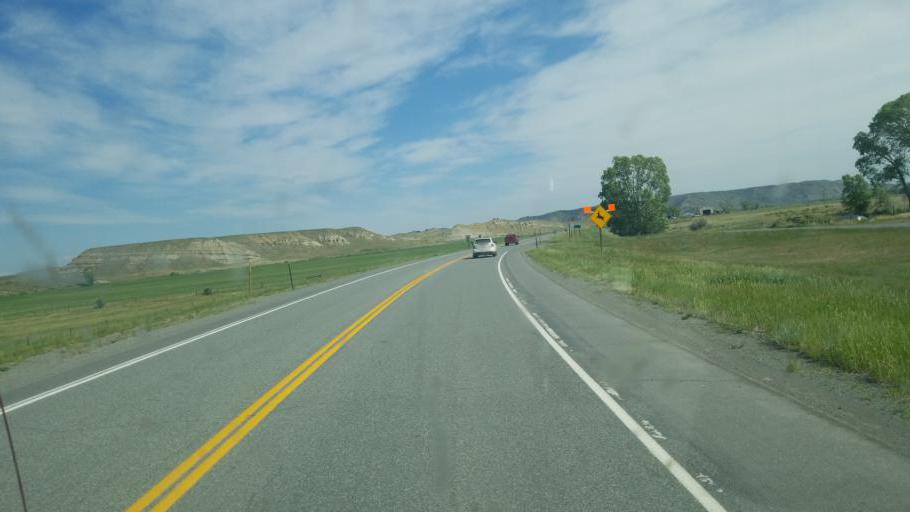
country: US
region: Wyoming
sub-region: Park County
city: Cody
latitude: 44.1618
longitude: -108.8759
